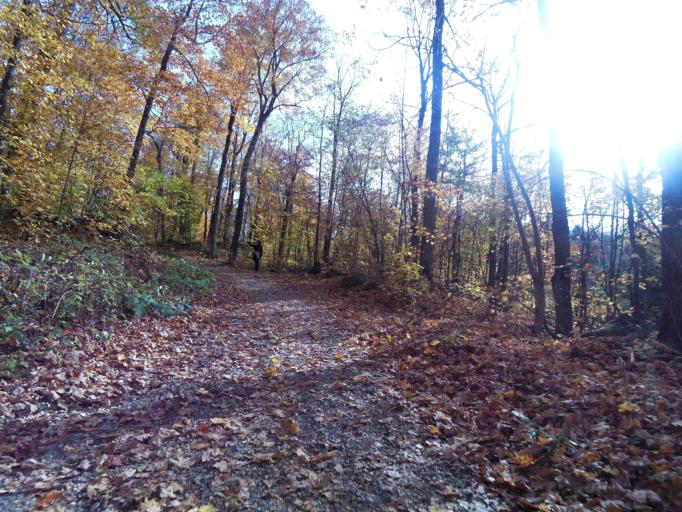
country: CA
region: Quebec
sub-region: Outaouais
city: Wakefield
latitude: 45.5025
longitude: -75.8697
